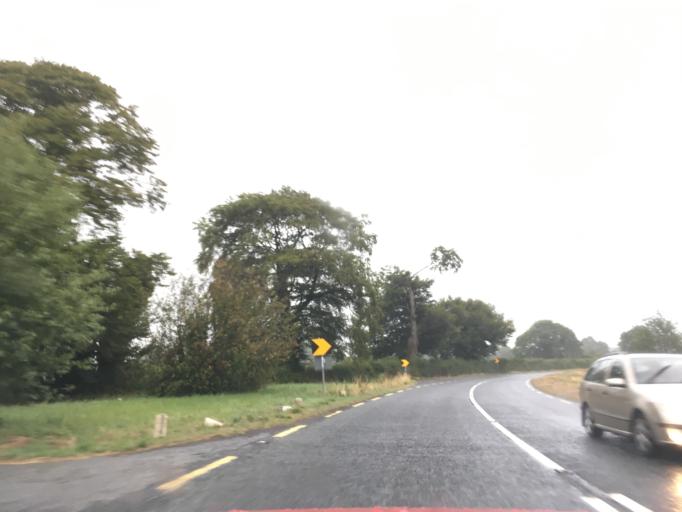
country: IE
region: Munster
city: Tipperary
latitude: 52.4816
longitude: -8.1088
